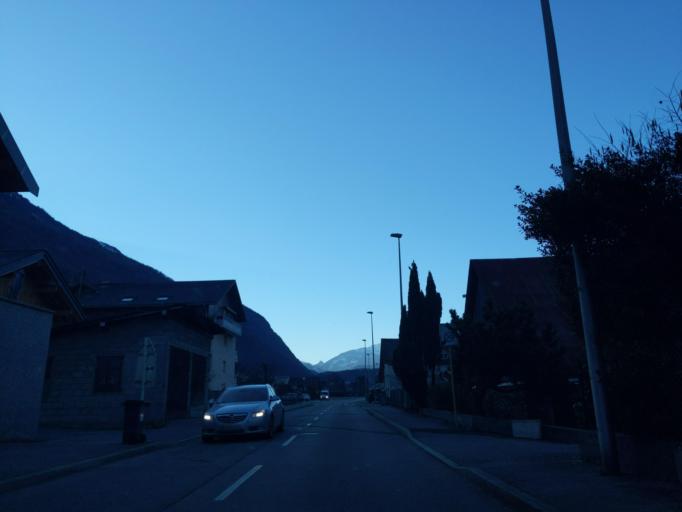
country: FR
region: Rhone-Alpes
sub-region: Departement de la Savoie
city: La Bathie
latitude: 45.6257
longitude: 6.4485
